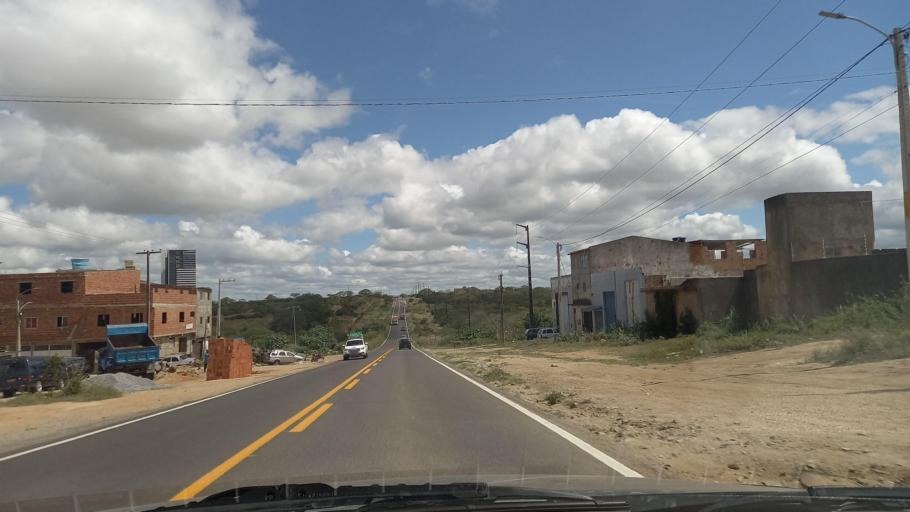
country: BR
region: Pernambuco
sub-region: Caruaru
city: Caruaru
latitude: -8.2573
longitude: -35.9570
